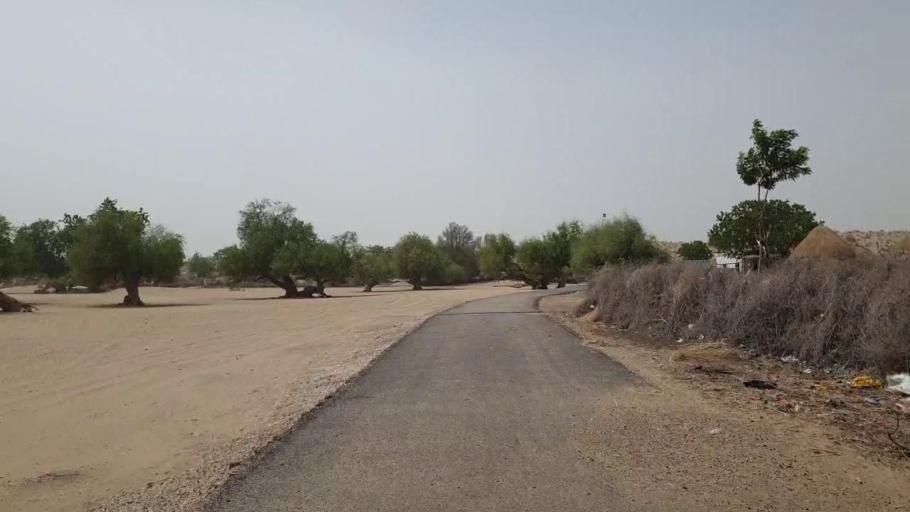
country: PK
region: Sindh
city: Islamkot
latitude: 24.7076
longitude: 70.6162
